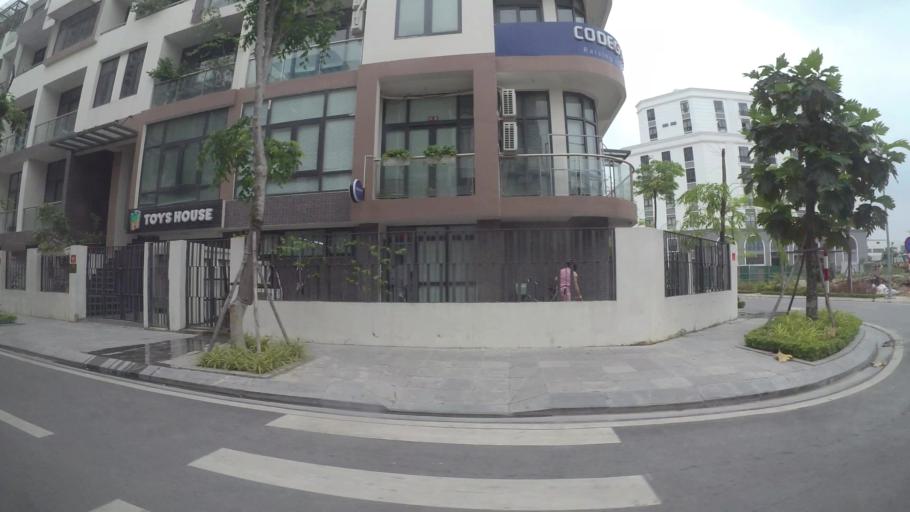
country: VN
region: Ha Noi
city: Cau Dien
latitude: 21.0356
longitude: 105.7682
